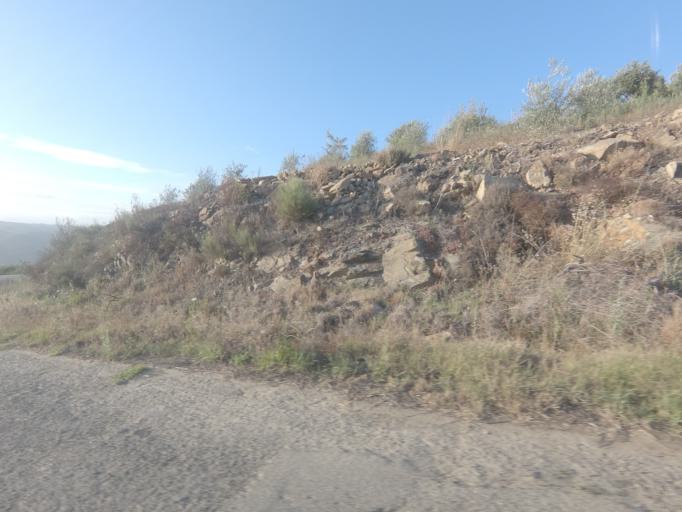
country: PT
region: Viseu
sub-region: Armamar
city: Armamar
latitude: 41.1246
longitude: -7.6719
